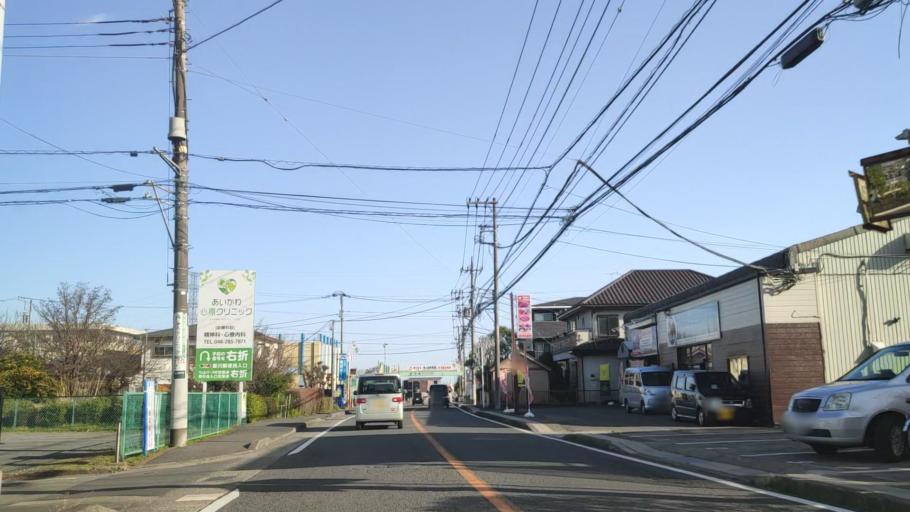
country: JP
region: Kanagawa
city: Zama
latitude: 35.5238
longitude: 139.3269
